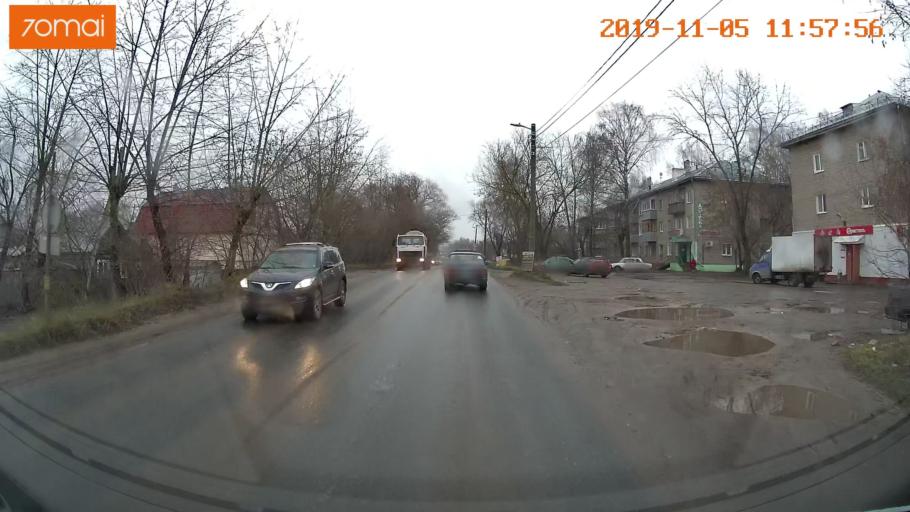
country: RU
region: Ivanovo
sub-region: Gorod Ivanovo
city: Ivanovo
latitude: 56.9819
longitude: 41.0376
